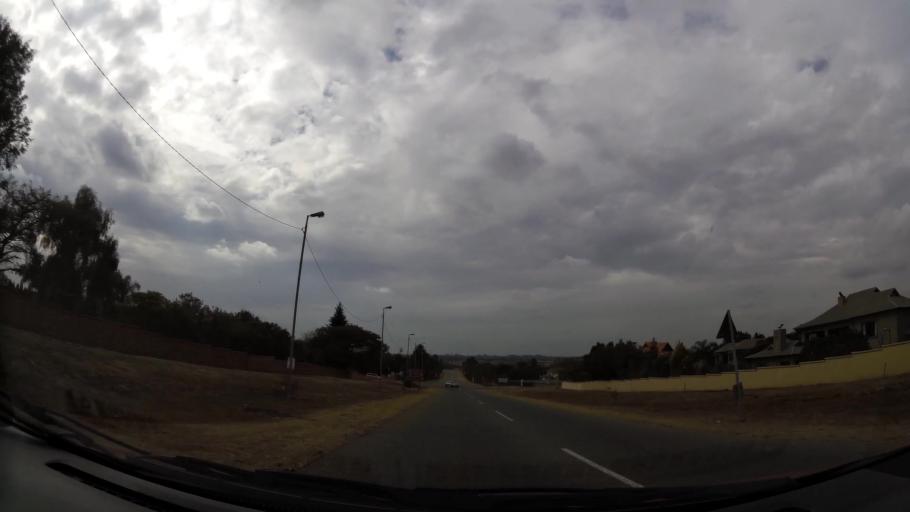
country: ZA
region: Gauteng
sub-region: West Rand District Municipality
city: Muldersdriseloop
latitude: -26.0780
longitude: 27.8597
